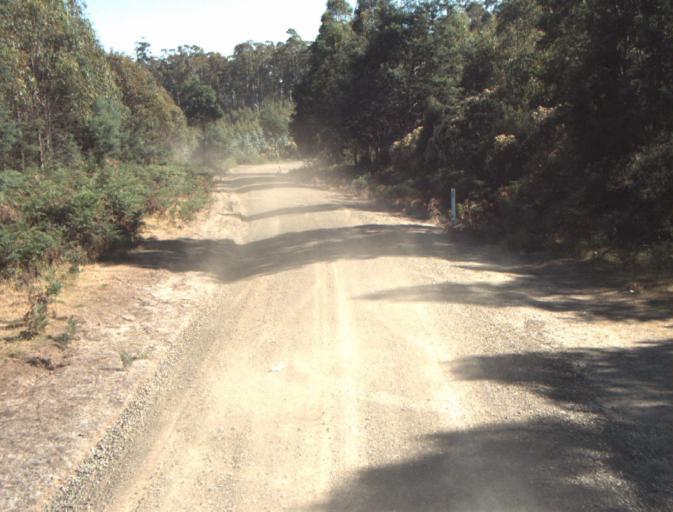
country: AU
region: Tasmania
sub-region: Dorset
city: Scottsdale
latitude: -41.2702
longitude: 147.3764
